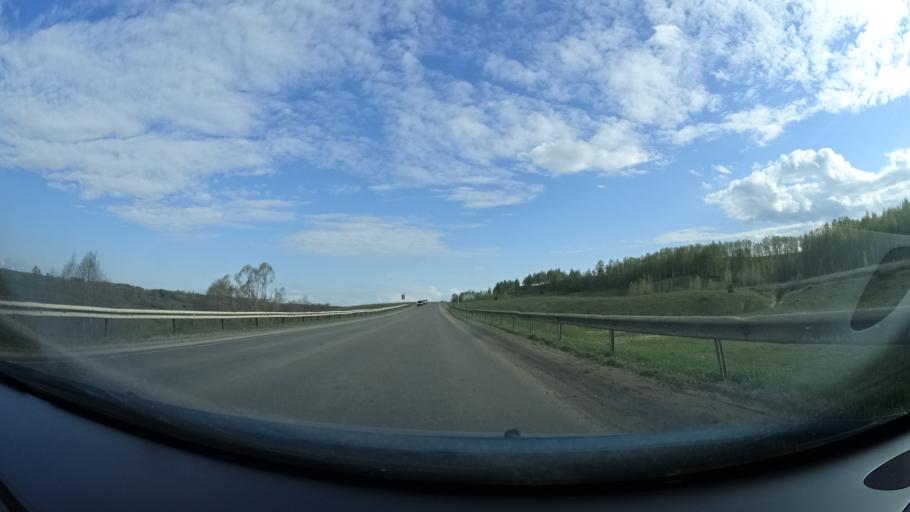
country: RU
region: Bashkortostan
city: Blagoveshchensk
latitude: 55.1134
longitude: 55.8414
